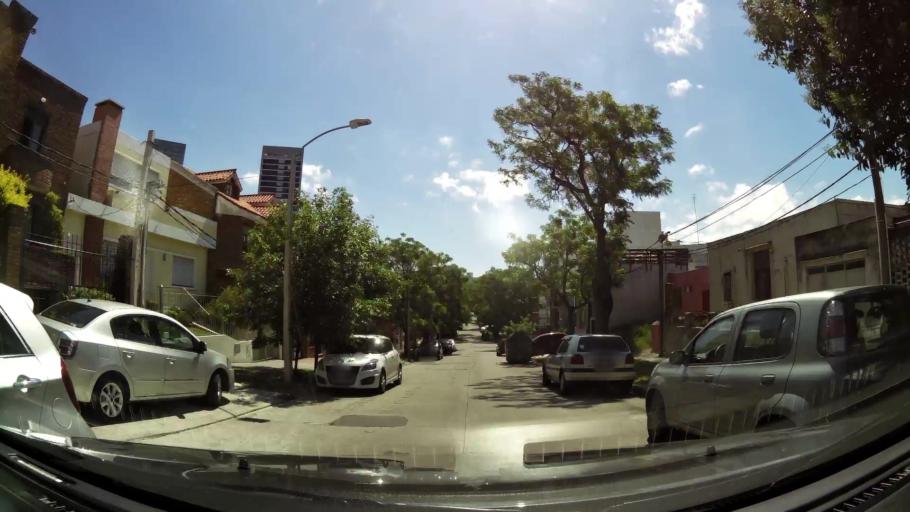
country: UY
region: Montevideo
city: Montevideo
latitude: -34.9021
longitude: -56.1318
